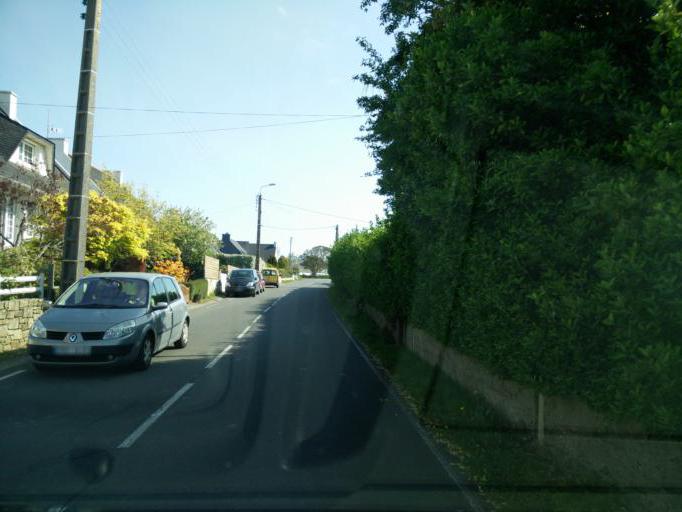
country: FR
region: Brittany
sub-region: Departement du Finistere
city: Crozon
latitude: 48.2433
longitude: -4.4840
